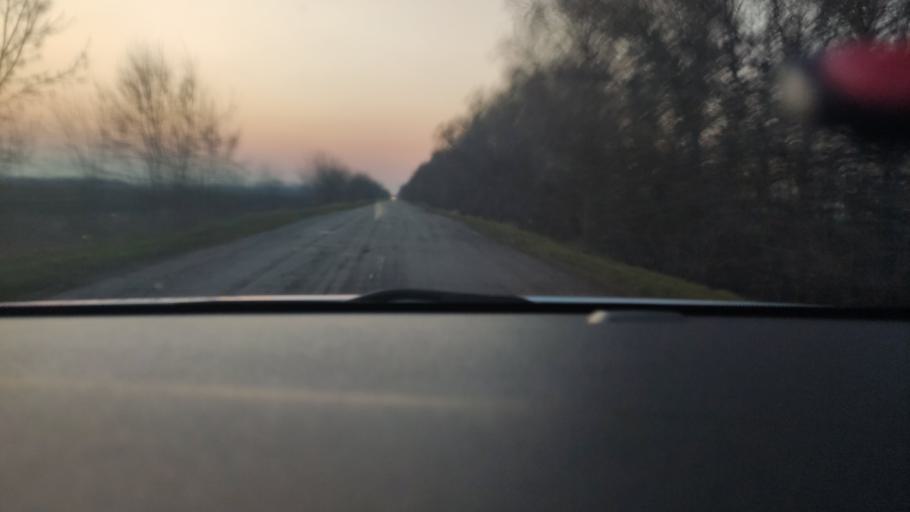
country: RU
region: Voronezj
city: Uryv-Pokrovka
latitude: 51.1376
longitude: 39.0836
